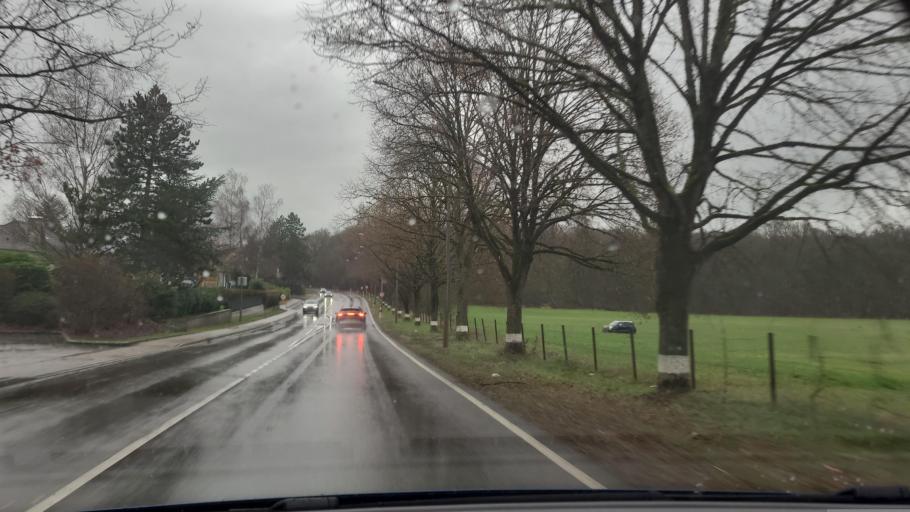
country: LU
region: Luxembourg
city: Capellen
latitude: 49.6428
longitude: 6.0026
